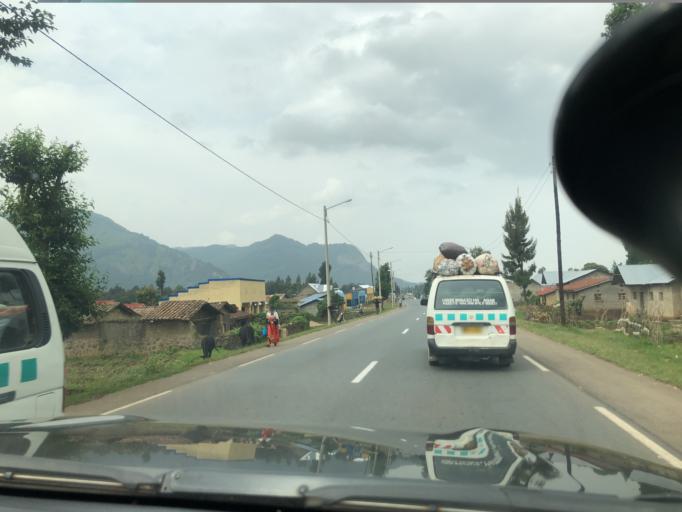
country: RW
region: Western Province
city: Gisenyi
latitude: -1.6330
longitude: 29.4132
